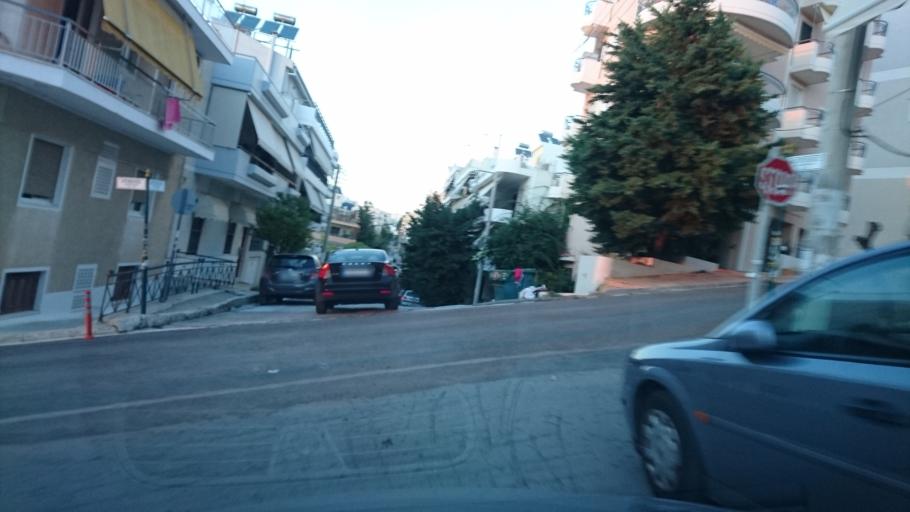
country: GR
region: Attica
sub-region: Nomarchia Athinas
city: Ilioupoli
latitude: 37.9380
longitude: 23.7654
